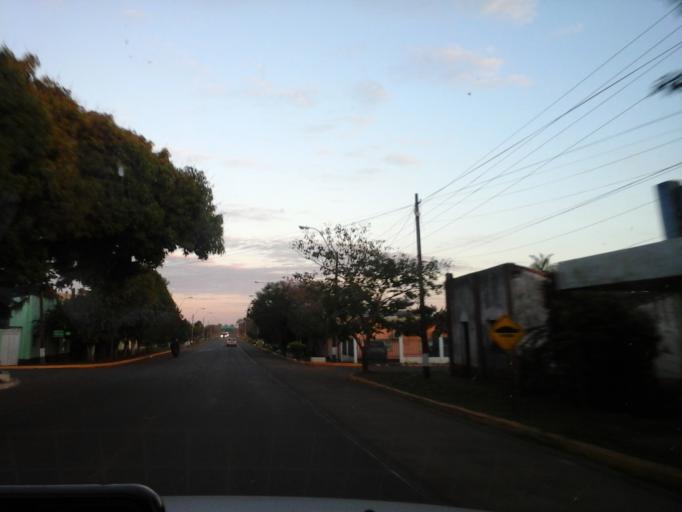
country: PY
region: Itapua
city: General Delgado
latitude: -27.0886
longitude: -56.5275
